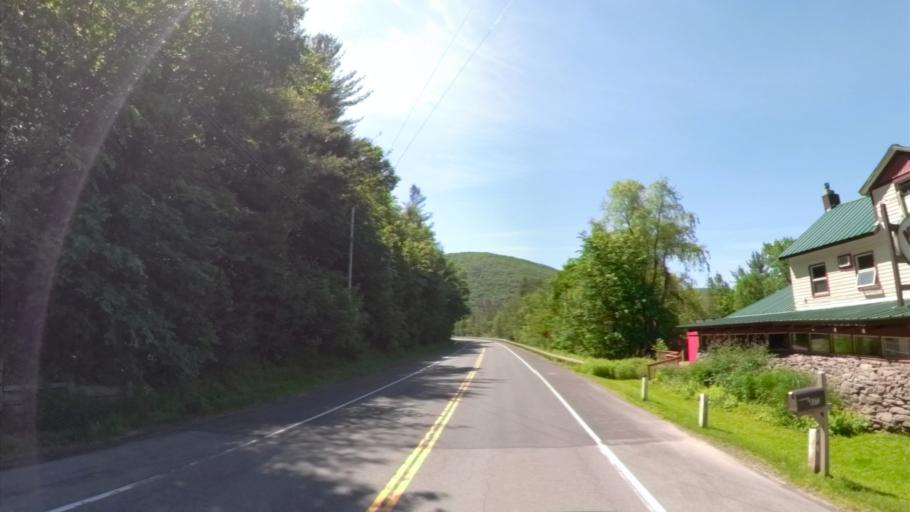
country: US
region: New York
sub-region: Ulster County
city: Shokan
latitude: 42.1077
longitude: -74.4504
